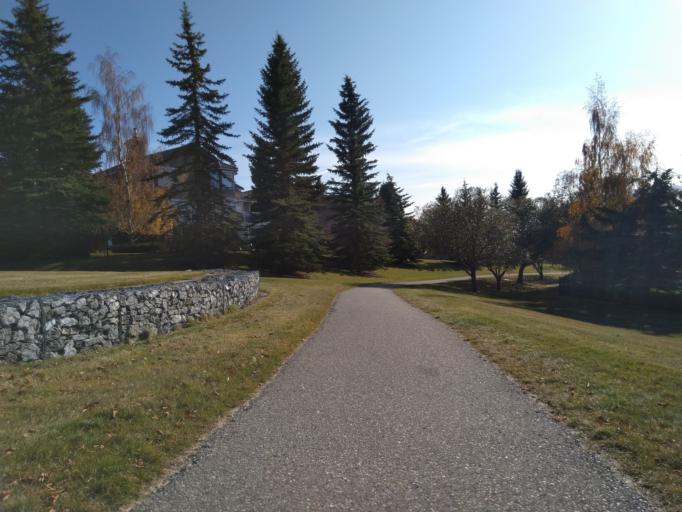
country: CA
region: Alberta
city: Calgary
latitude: 51.1304
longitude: -114.1512
